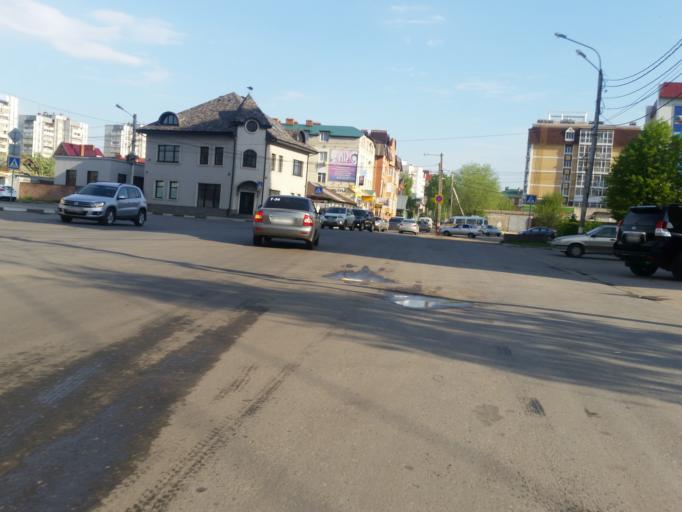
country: RU
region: Ulyanovsk
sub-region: Ulyanovskiy Rayon
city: Ulyanovsk
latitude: 54.3278
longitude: 48.3968
